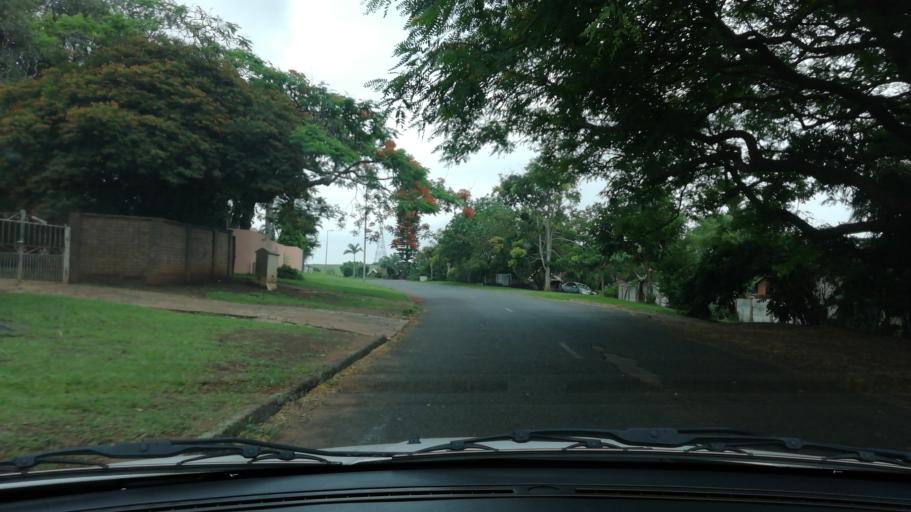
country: ZA
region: KwaZulu-Natal
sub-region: uThungulu District Municipality
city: Empangeni
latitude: -28.7366
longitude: 31.9025
